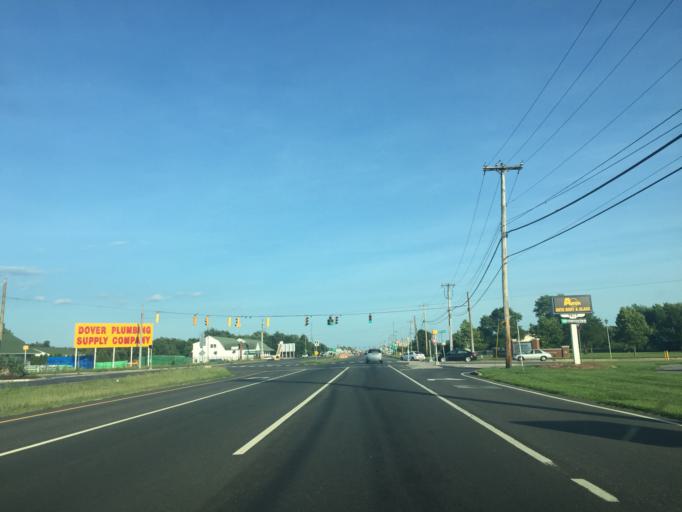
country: US
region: Delaware
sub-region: Kent County
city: Cheswold
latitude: 39.2029
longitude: -75.5599
